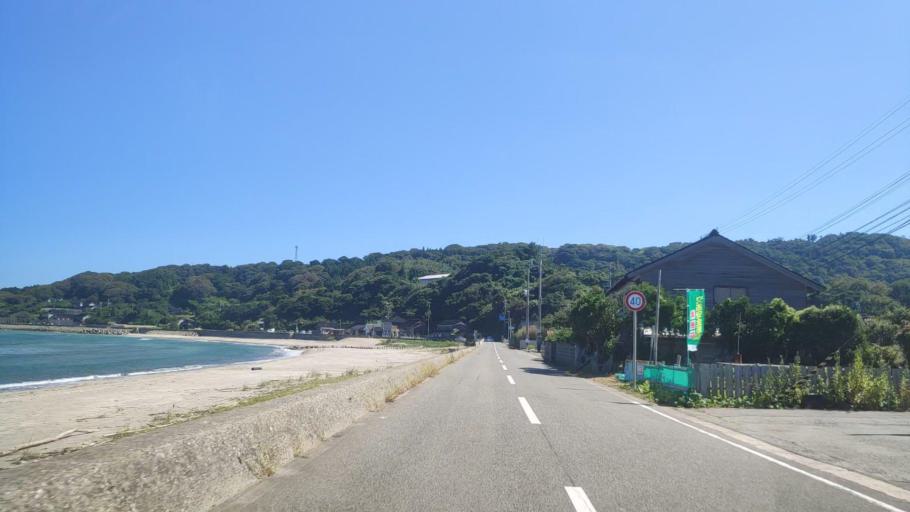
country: JP
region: Ishikawa
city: Nanao
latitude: 37.5275
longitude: 137.2802
